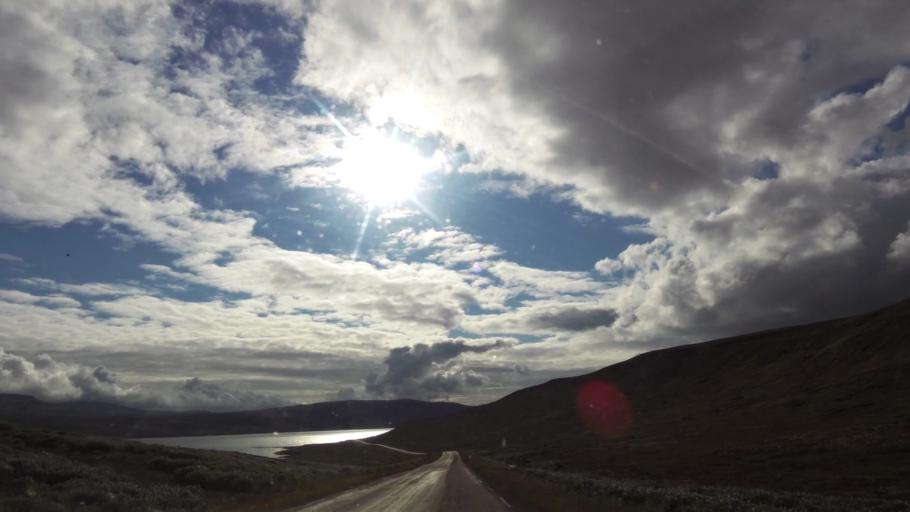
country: IS
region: West
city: Olafsvik
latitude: 65.5385
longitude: -23.8308
